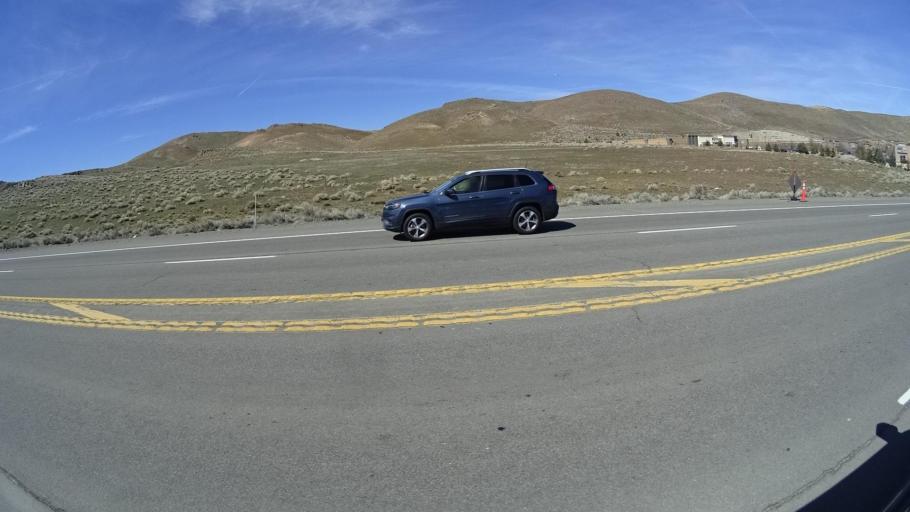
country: US
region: Nevada
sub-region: Washoe County
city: Sun Valley
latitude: 39.5802
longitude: -119.7445
